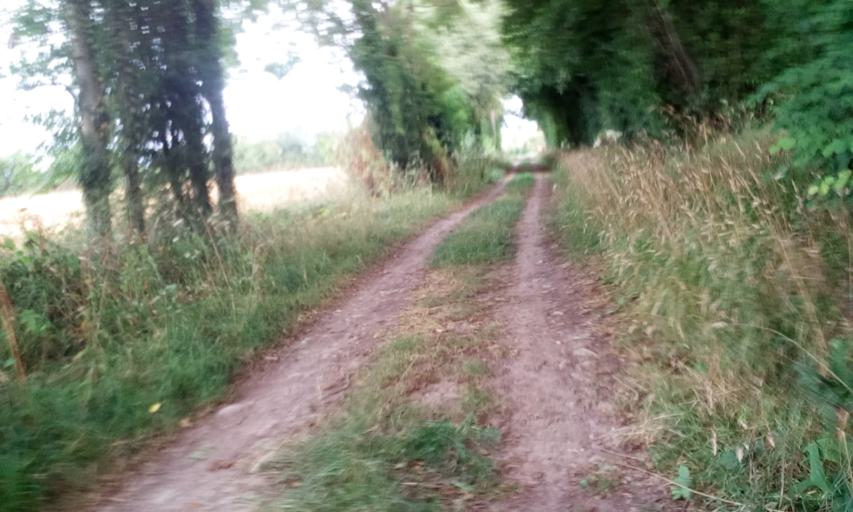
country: FR
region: Lower Normandy
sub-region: Departement du Calvados
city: Merville-Franceville-Plage
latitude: 49.2527
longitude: -0.2023
